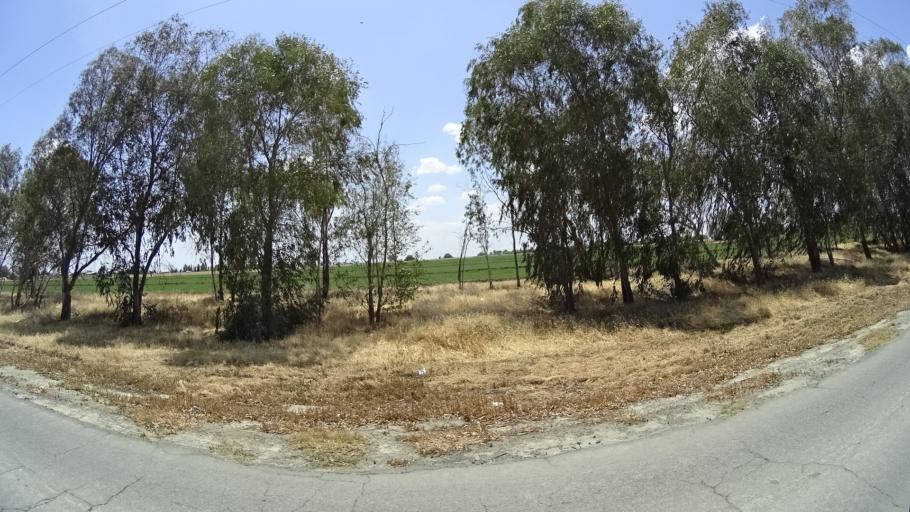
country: US
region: California
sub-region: Kings County
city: Stratford
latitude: 36.1894
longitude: -119.8328
